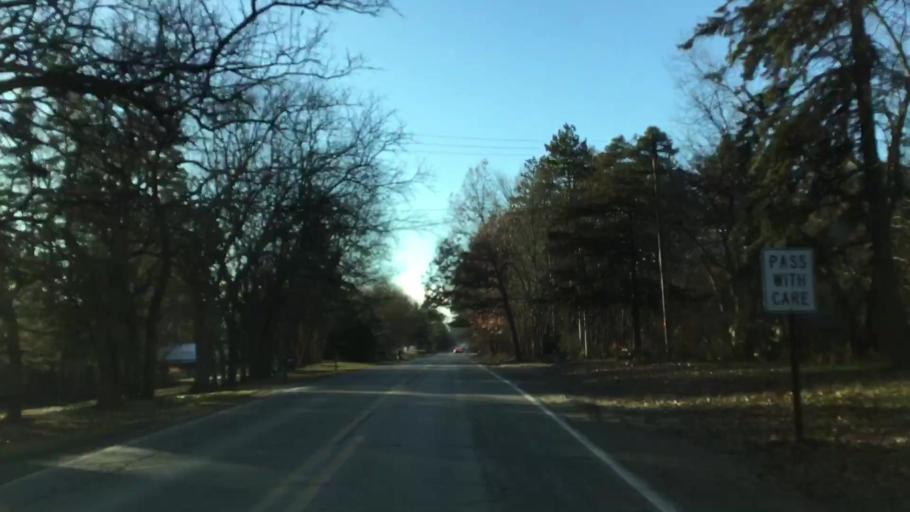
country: US
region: Michigan
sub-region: Genesee County
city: Linden
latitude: 42.7768
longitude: -83.7821
